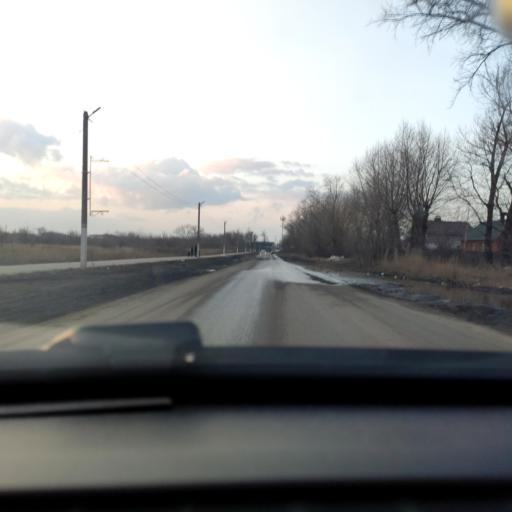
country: RU
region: Voronezj
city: Somovo
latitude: 51.6726
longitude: 39.3237
